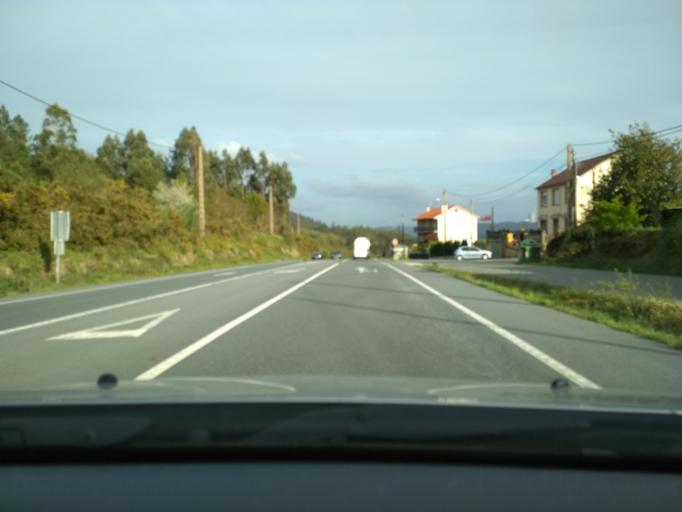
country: ES
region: Galicia
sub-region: Provincia da Coruna
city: Cerceda
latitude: 43.2275
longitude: -8.4652
